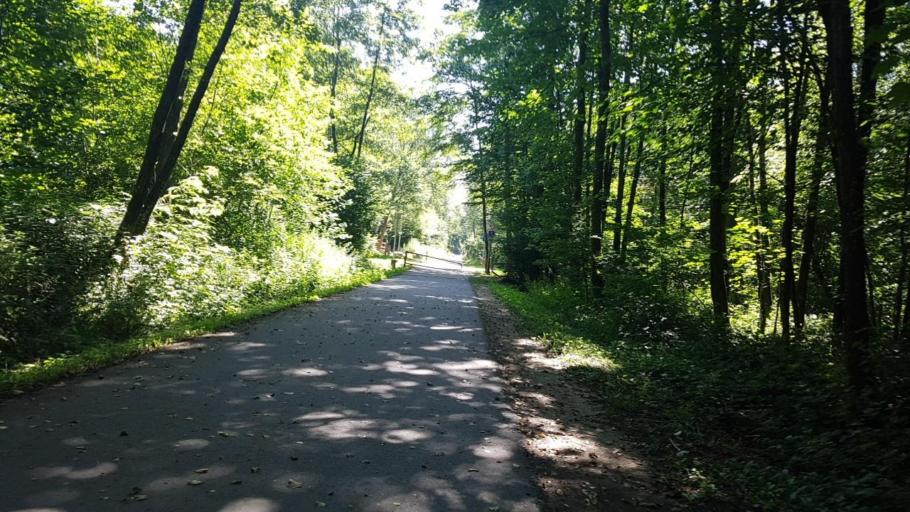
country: BE
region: Wallonia
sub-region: Province du Hainaut
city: Momignies
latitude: 50.0258
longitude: 4.2014
